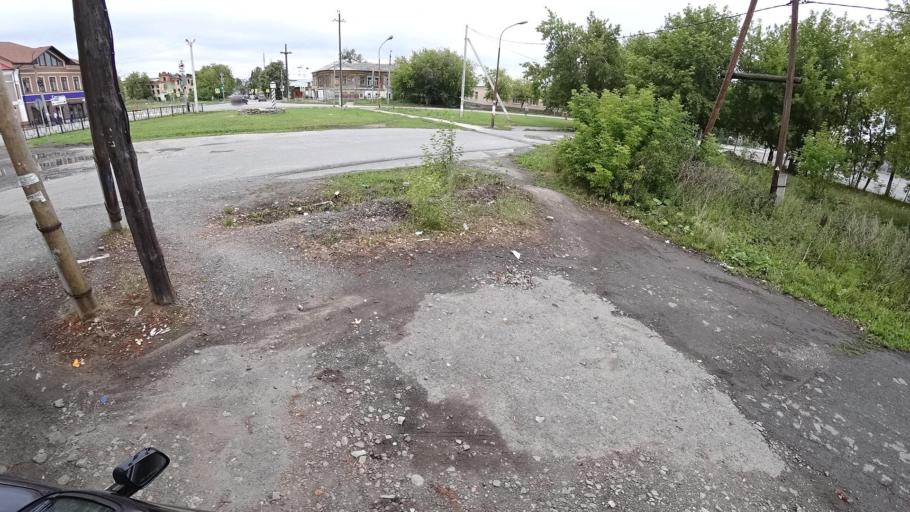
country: RU
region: Sverdlovsk
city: Kamyshlov
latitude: 56.8465
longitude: 62.7133
